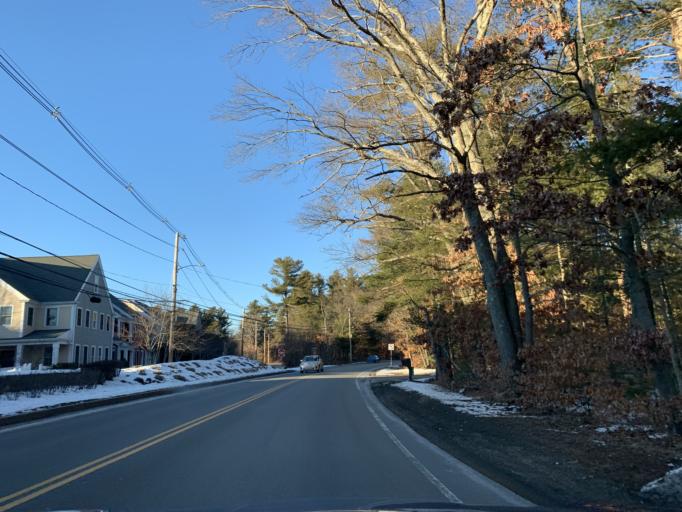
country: US
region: Massachusetts
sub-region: Bristol County
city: Norton Center
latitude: 41.9928
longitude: -71.1552
